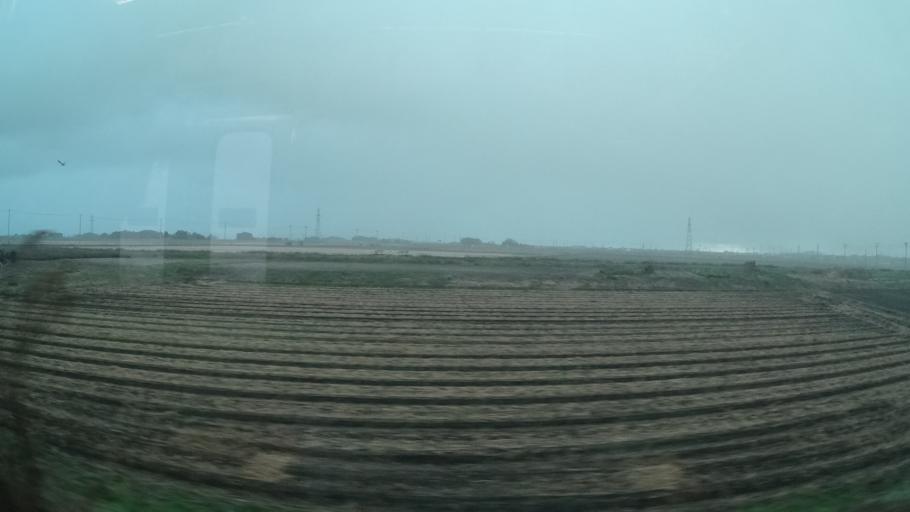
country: JP
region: Miyagi
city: Watari
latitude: 38.0443
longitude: 140.8581
